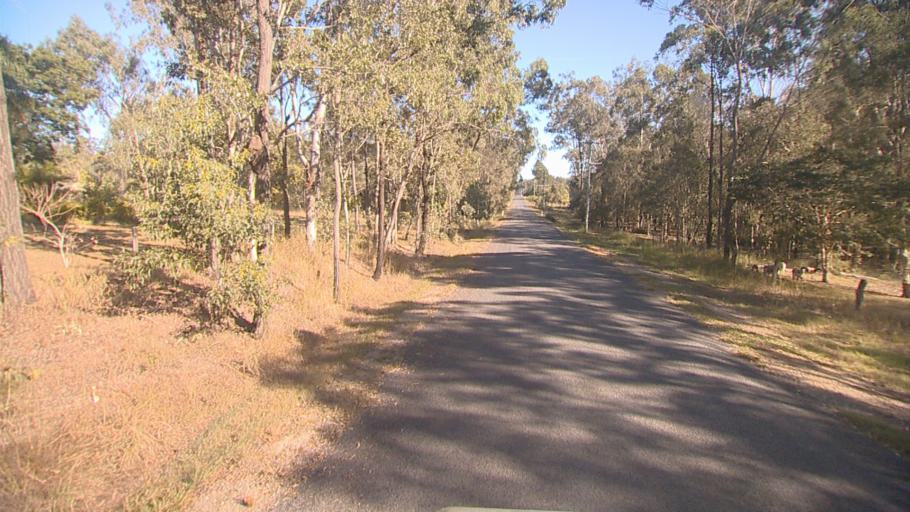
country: AU
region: Queensland
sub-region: Ipswich
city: Springfield Lakes
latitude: -27.6920
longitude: 152.9432
